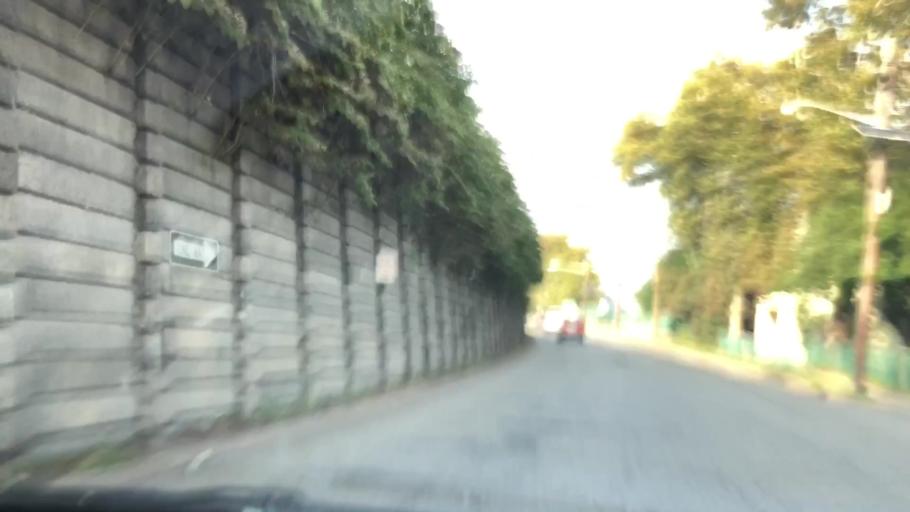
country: US
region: New Jersey
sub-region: Essex County
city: Bloomfield
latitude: 40.7908
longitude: -74.1933
